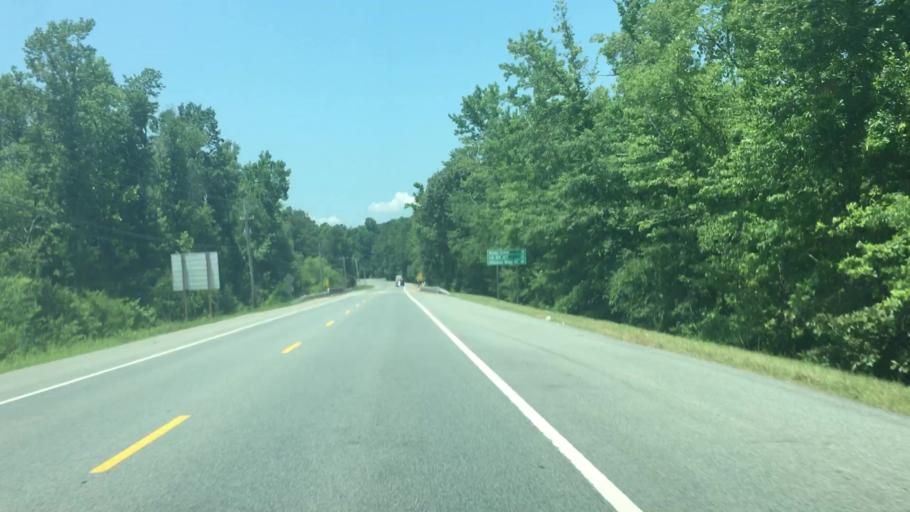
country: US
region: Maryland
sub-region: Saint Mary's County
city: Mechanicsville
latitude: 38.3694
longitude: -76.7835
